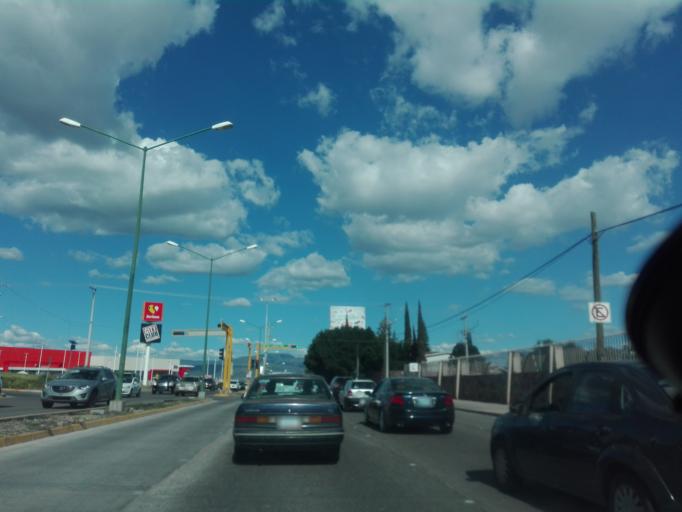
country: MX
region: Guanajuato
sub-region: Leon
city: La Ermita
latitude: 21.1546
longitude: -101.7107
